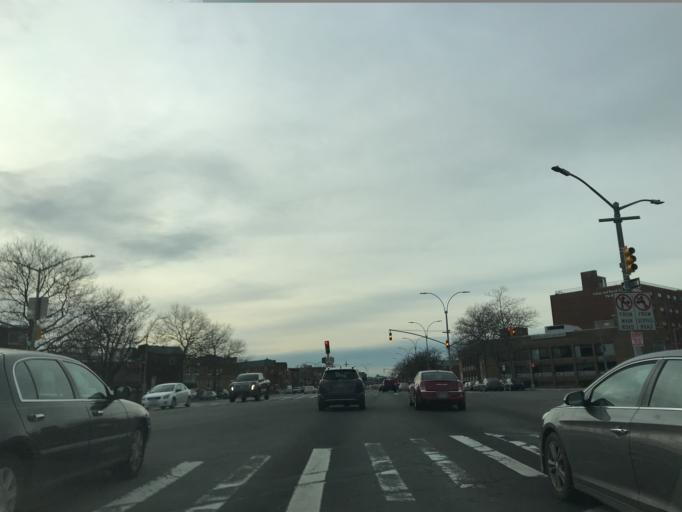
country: US
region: New York
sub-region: Kings County
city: East New York
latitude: 40.6542
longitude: -73.9118
